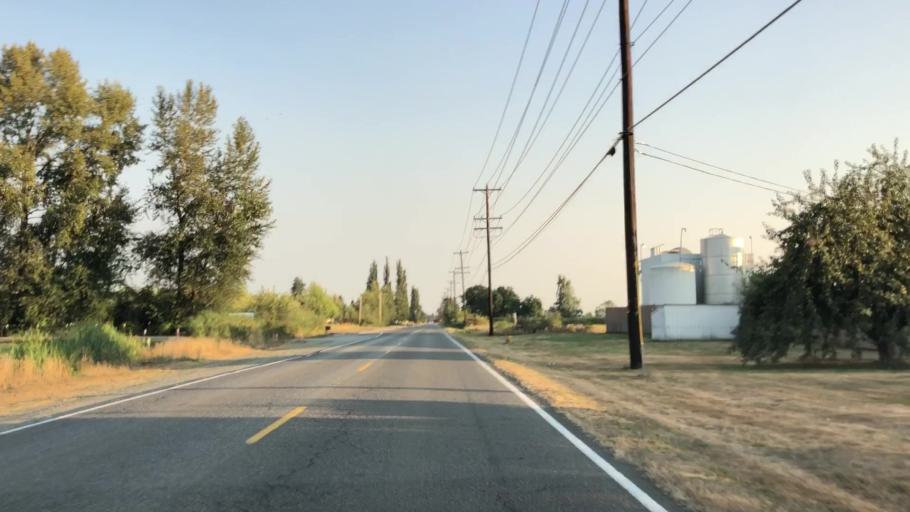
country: US
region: Washington
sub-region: Snohomish County
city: Smokey Point
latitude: 48.1492
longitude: -122.1616
